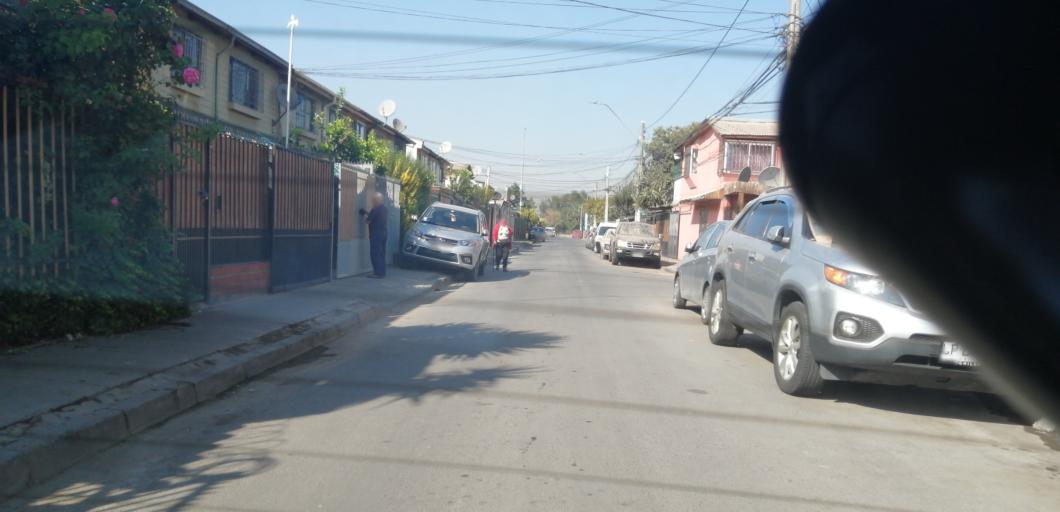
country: CL
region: Santiago Metropolitan
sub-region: Provincia de Santiago
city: Lo Prado
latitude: -33.4638
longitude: -70.7477
